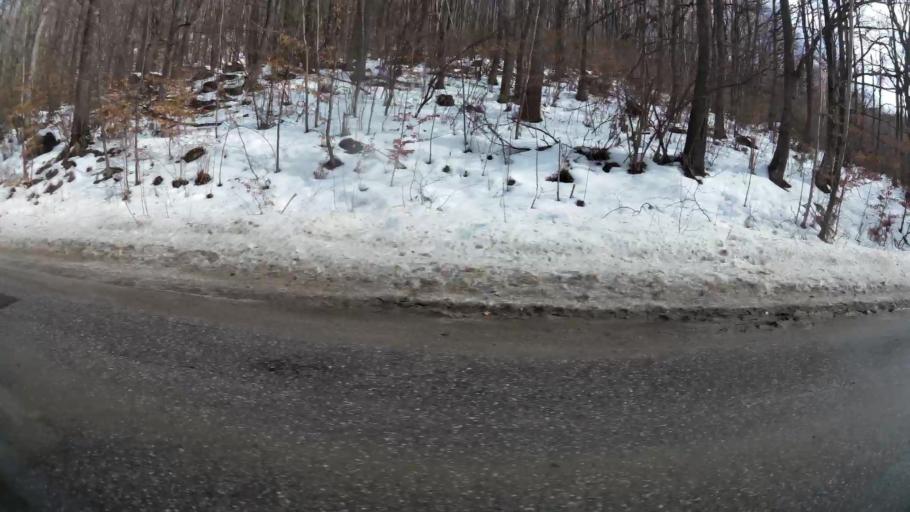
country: BG
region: Sofia-Capital
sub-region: Stolichna Obshtina
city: Sofia
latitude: 42.6325
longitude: 23.2287
